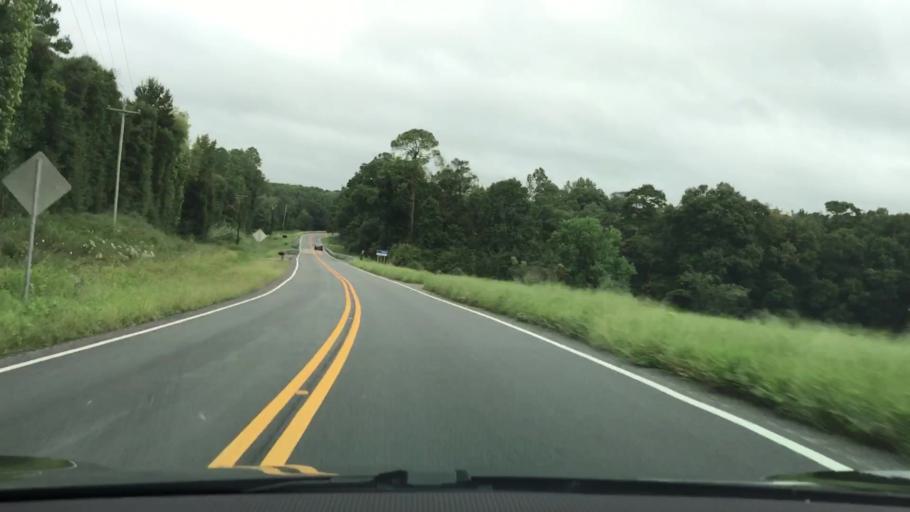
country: US
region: Alabama
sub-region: Covington County
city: Opp
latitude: 31.2240
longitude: -86.1603
